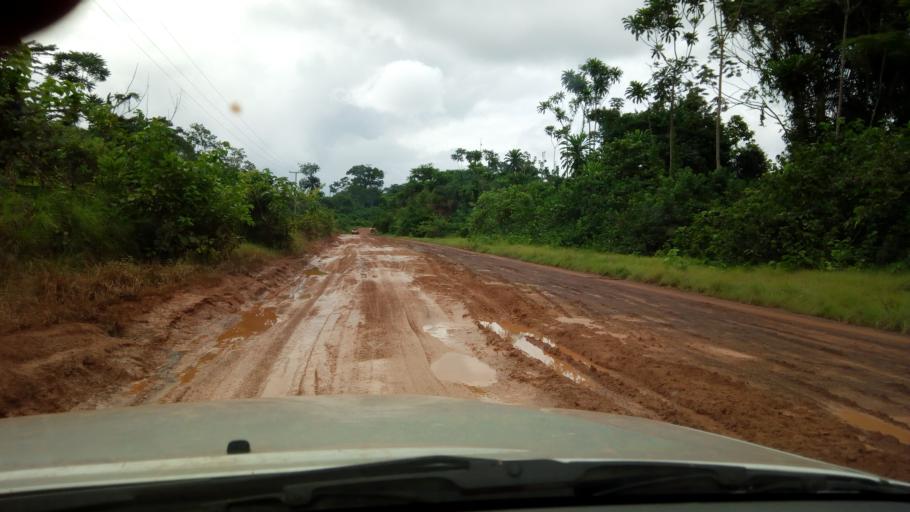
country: LR
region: Grand Gedeh
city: Zwedru
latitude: 6.2005
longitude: -8.3564
